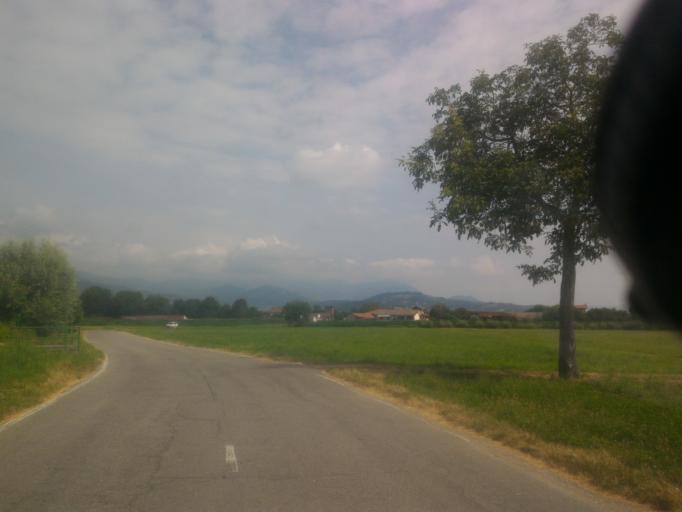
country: IT
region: Piedmont
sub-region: Provincia di Torino
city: San Secondo di Pinerolo
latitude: 44.8593
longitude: 7.3204
